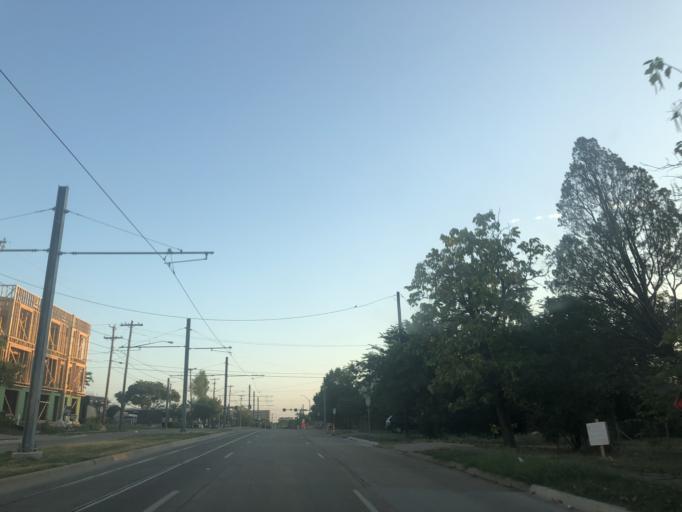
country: US
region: Texas
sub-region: Dallas County
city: Dallas
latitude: 32.7514
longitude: -96.8240
